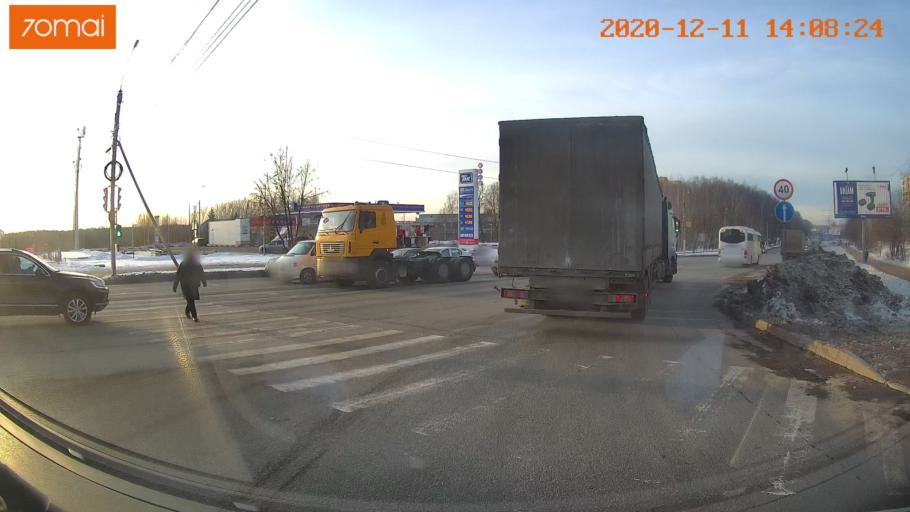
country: RU
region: Kostroma
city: Oktyabr'skiy
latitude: 57.7362
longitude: 40.9958
